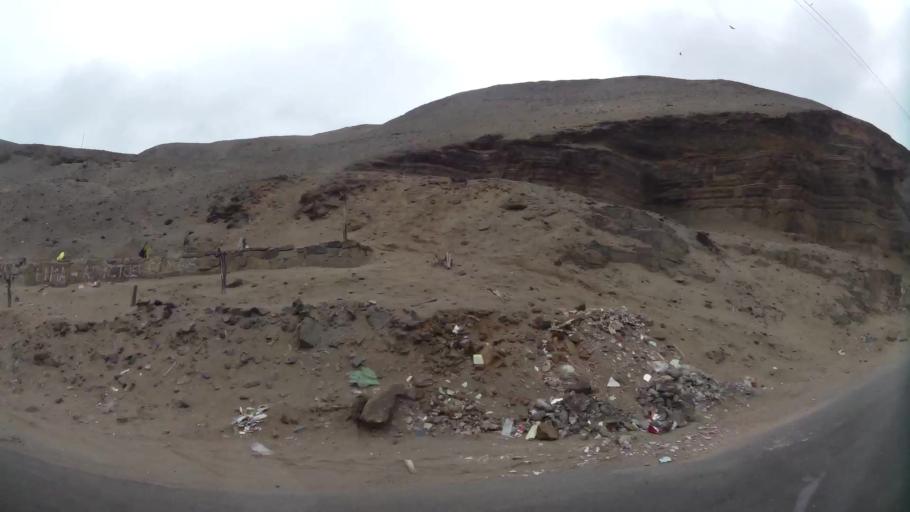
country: PE
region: Lima
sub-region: Lima
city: Surco
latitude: -12.1716
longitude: -77.0346
